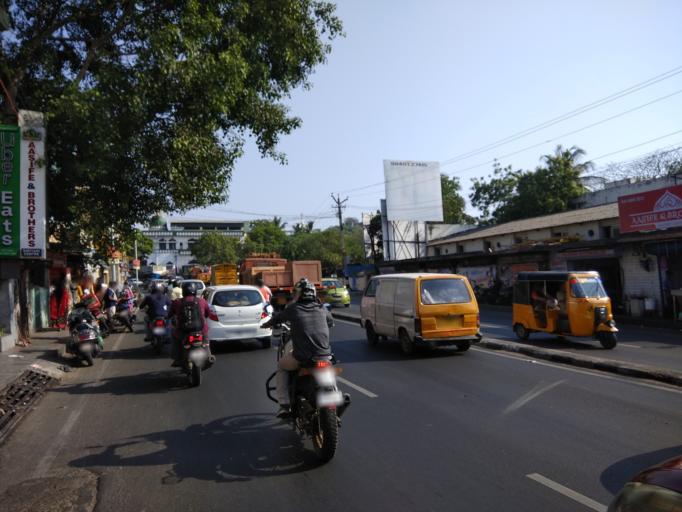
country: IN
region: Tamil Nadu
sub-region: Kancheepuram
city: Saint Thomas Mount
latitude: 13.0102
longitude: 80.1960
